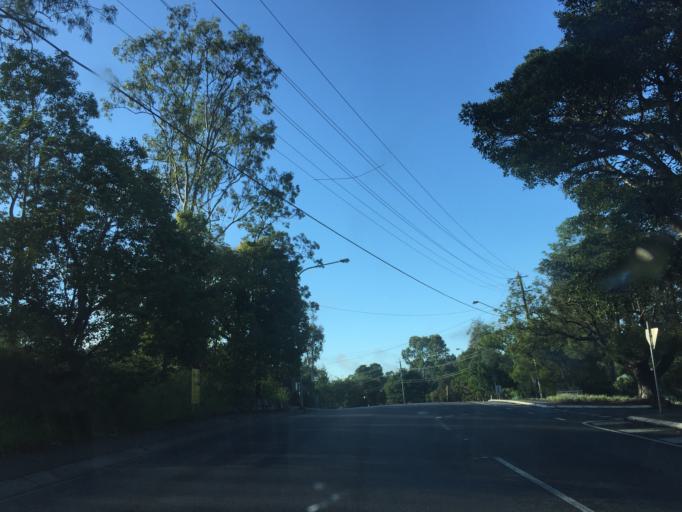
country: AU
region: Queensland
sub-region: Moreton Bay
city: Ferny Hills
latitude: -27.4421
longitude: 152.9398
